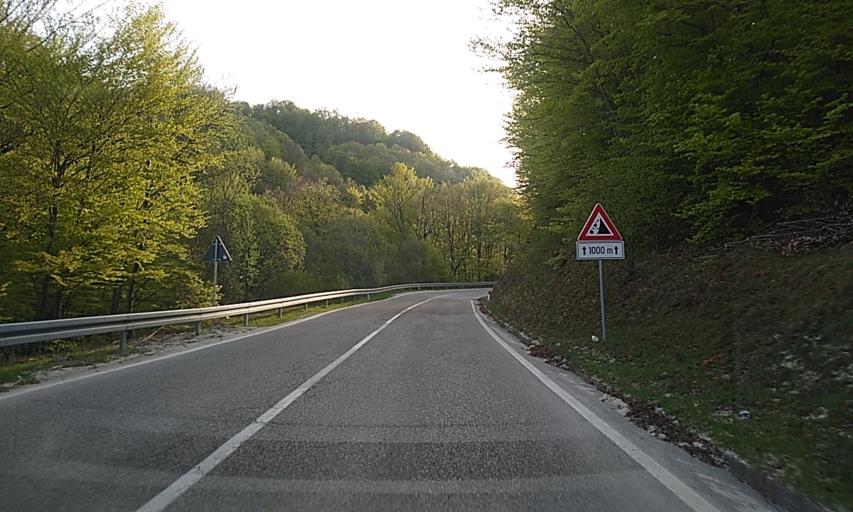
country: RS
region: Central Serbia
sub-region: Pcinjski Okrug
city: Surdulica
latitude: 42.6618
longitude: 22.2999
